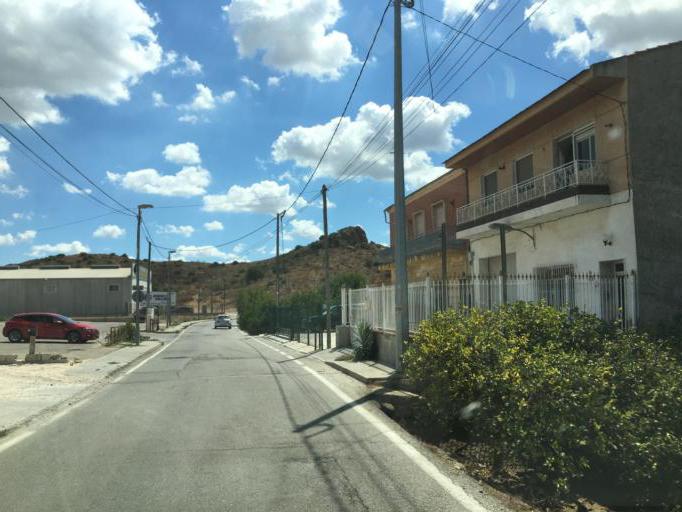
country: ES
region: Murcia
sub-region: Murcia
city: Santomera
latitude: 38.0536
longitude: -1.0688
